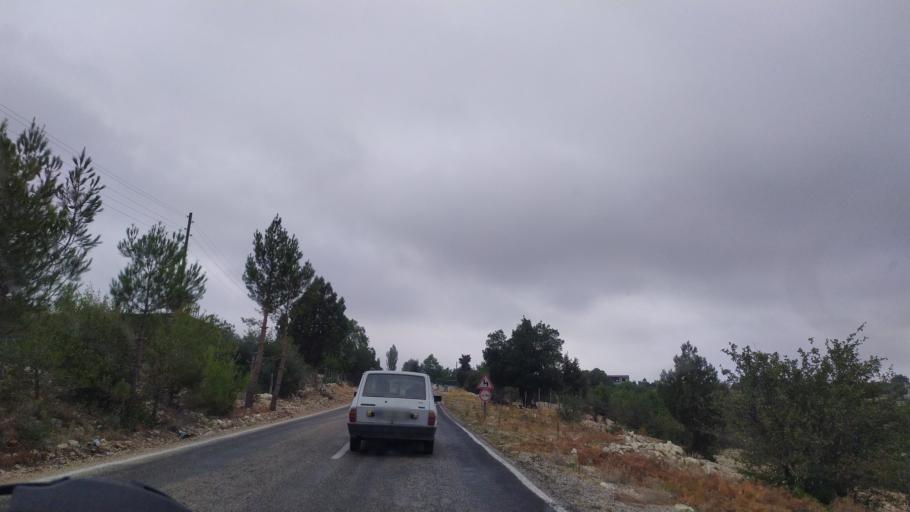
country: TR
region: Mersin
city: Silifke
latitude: 36.5483
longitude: 33.9217
